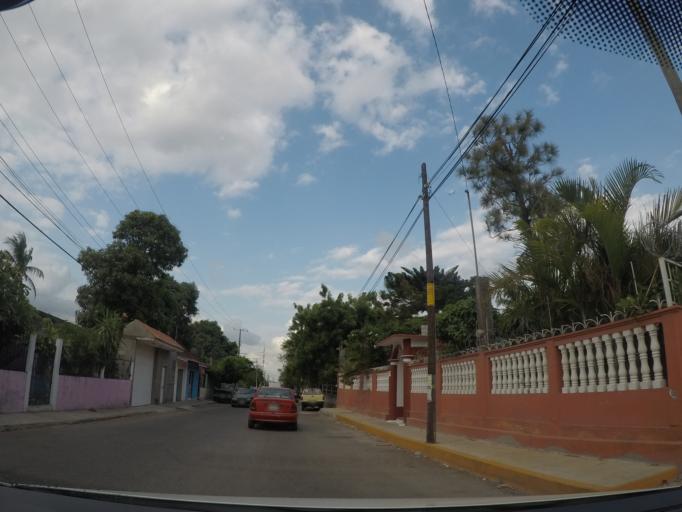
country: MX
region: Oaxaca
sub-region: Salina Cruz
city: Salina Cruz
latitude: 16.2073
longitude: -95.2071
